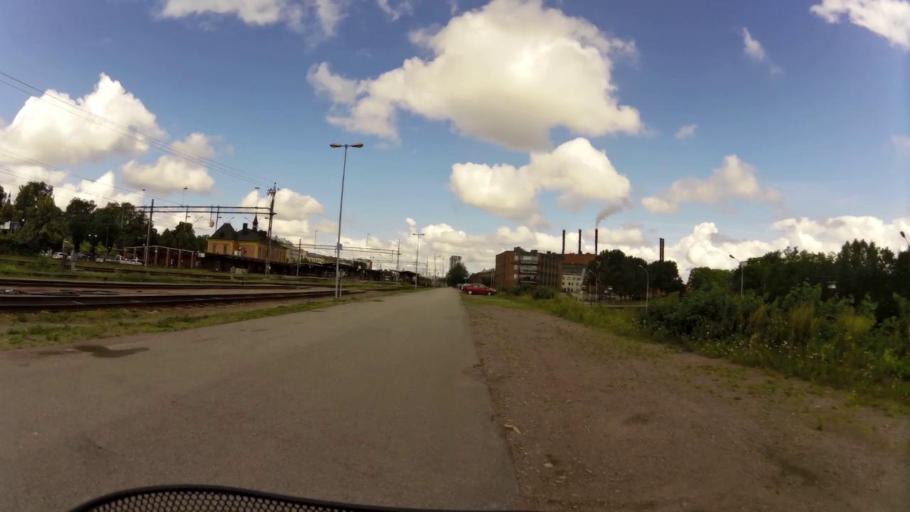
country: SE
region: OEstergoetland
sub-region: Linkopings Kommun
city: Linkoping
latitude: 58.4157
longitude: 15.6282
